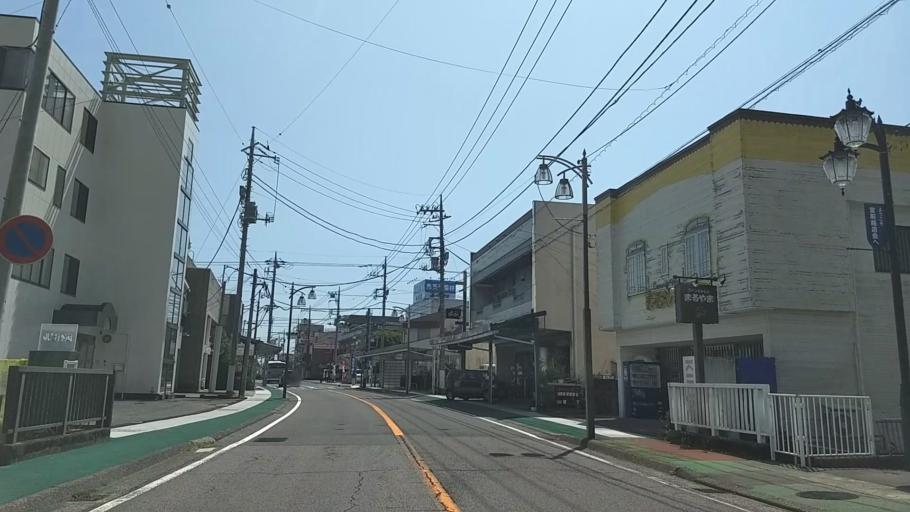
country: JP
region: Shizuoka
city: Gotemba
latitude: 35.2998
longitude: 138.9313
